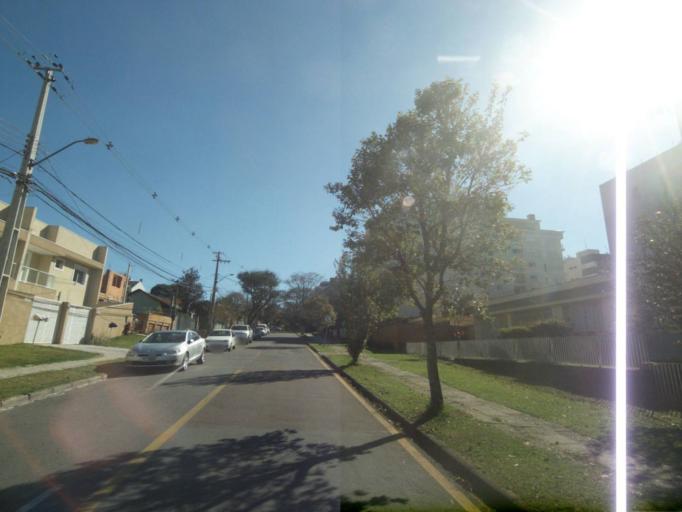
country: BR
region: Parana
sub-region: Curitiba
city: Curitiba
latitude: -25.3996
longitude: -49.2414
